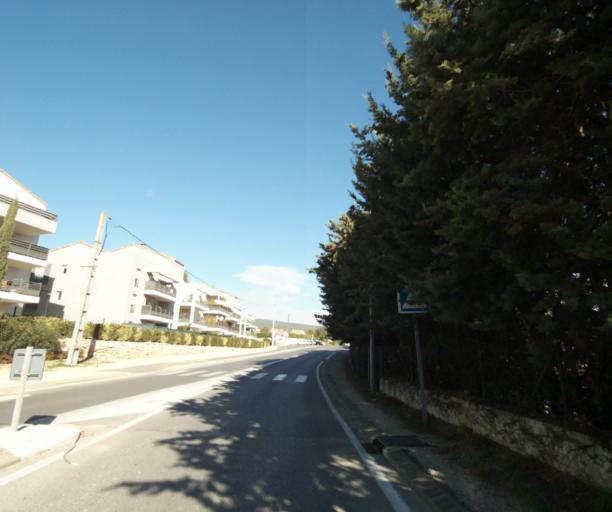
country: FR
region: Provence-Alpes-Cote d'Azur
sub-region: Departement des Bouches-du-Rhone
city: Ceyreste
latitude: 43.2017
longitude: 5.6236
